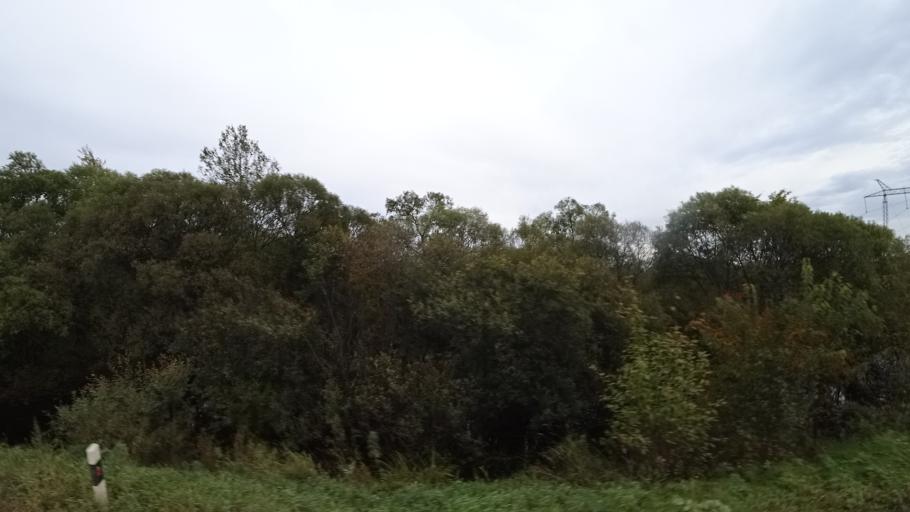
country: RU
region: Amur
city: Arkhara
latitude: 49.4309
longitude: 130.2518
